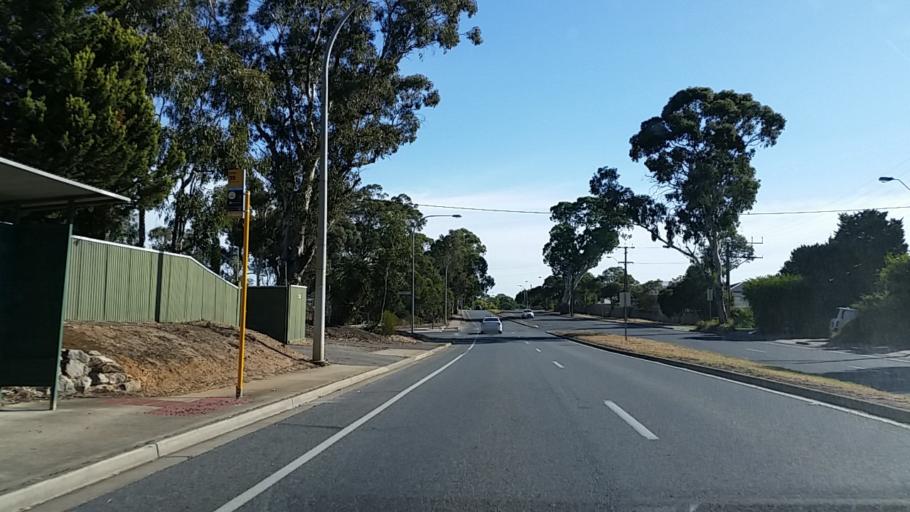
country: AU
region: South Australia
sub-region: Tea Tree Gully
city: Hope Valley
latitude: -34.8503
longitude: 138.7137
